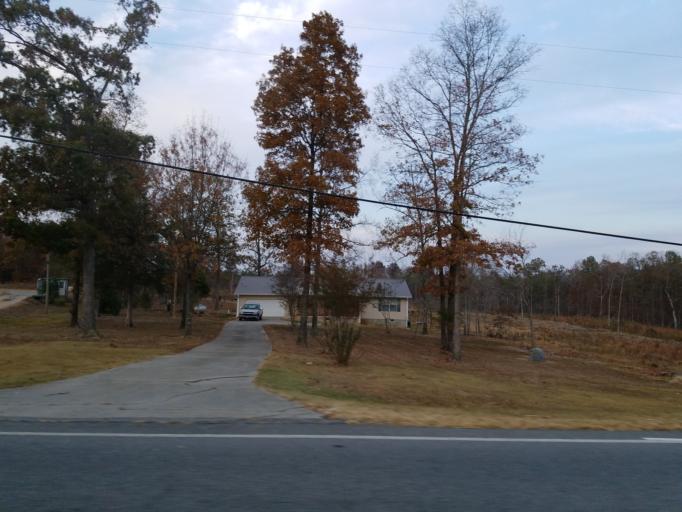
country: US
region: Georgia
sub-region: Murray County
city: Chatsworth
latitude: 34.6051
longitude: -84.8026
